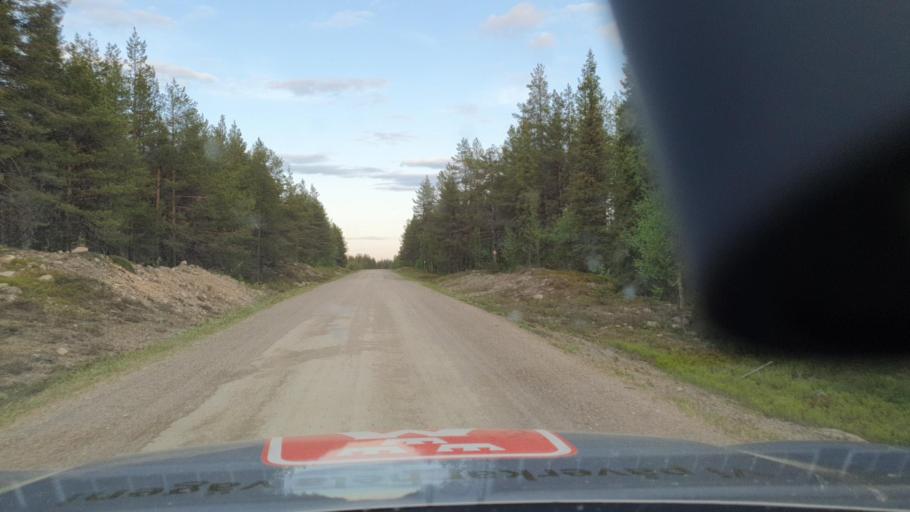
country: SE
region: Norrbotten
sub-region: Bodens Kommun
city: Boden
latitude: 66.5780
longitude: 21.4127
